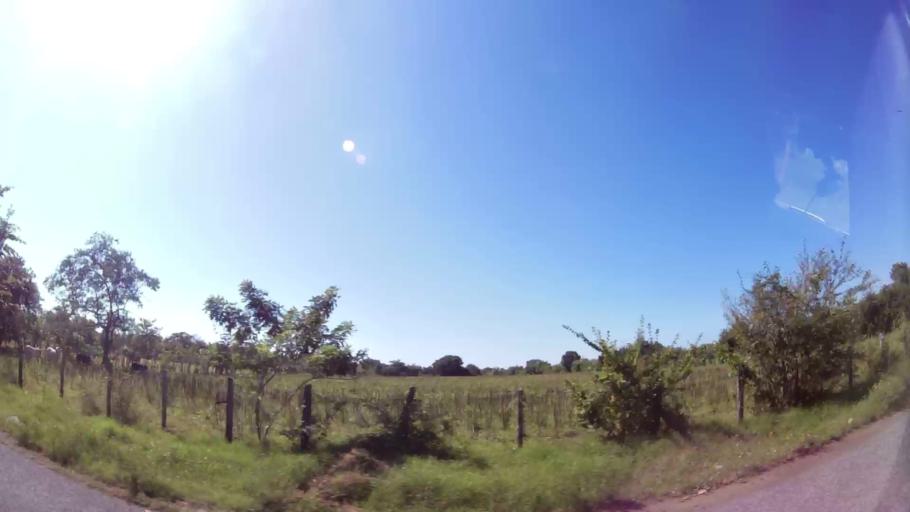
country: GT
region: Santa Rosa
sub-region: Municipio de Taxisco
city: Taxisco
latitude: 13.9090
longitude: -90.5239
